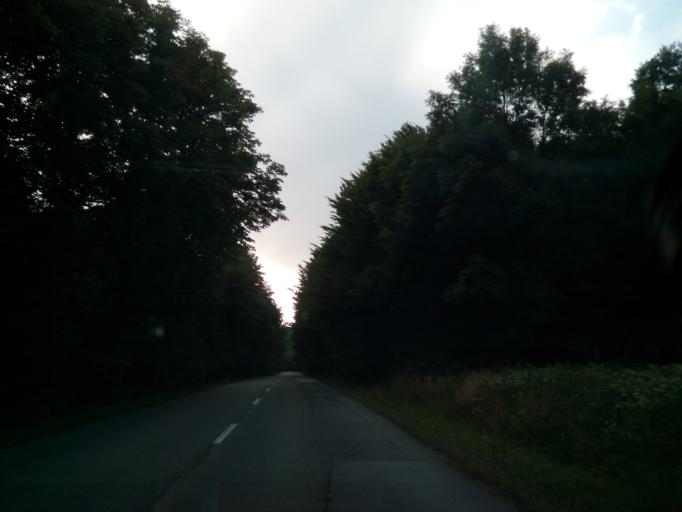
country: SK
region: Kosicky
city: Kosice
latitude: 48.6346
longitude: 21.4505
